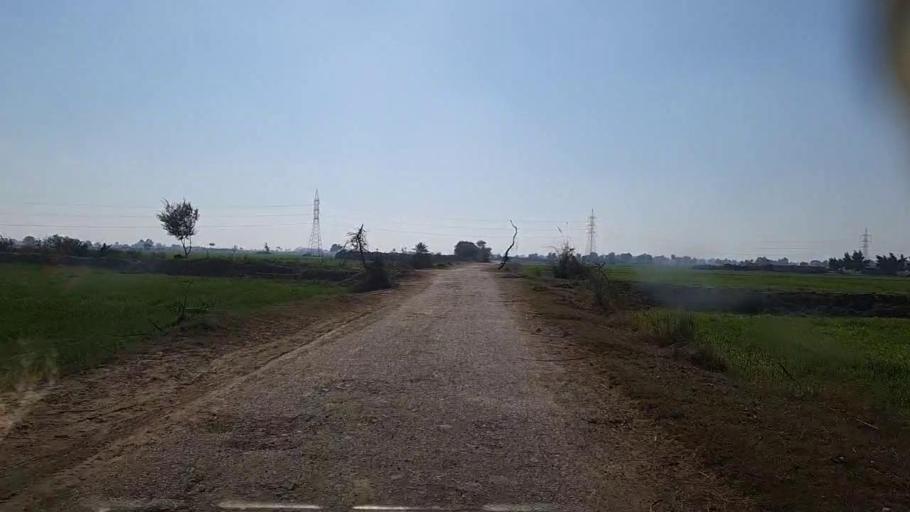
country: PK
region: Sindh
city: Khairpur
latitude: 28.0428
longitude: 69.7826
